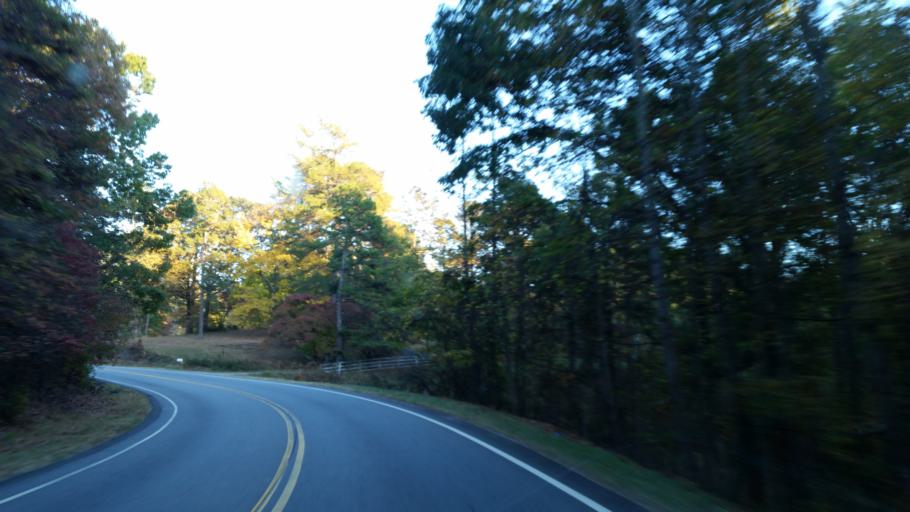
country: US
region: Georgia
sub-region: Lumpkin County
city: Dahlonega
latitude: 34.5248
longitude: -84.0324
